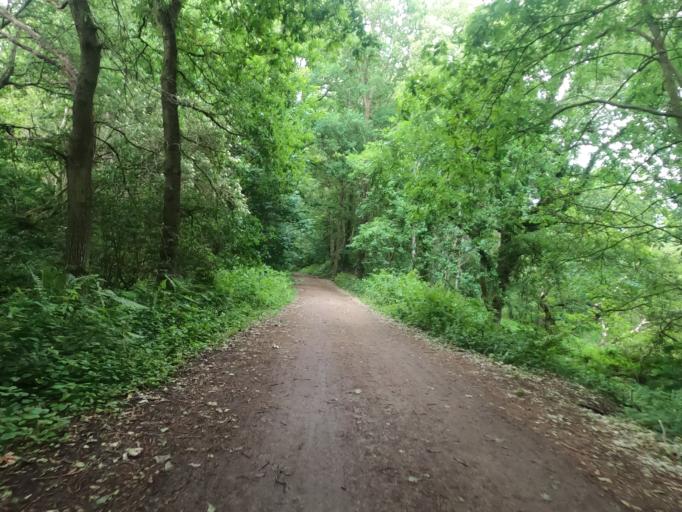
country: GB
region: England
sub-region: Cheshire West and Chester
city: Cuddington
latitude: 53.2313
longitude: -2.6173
